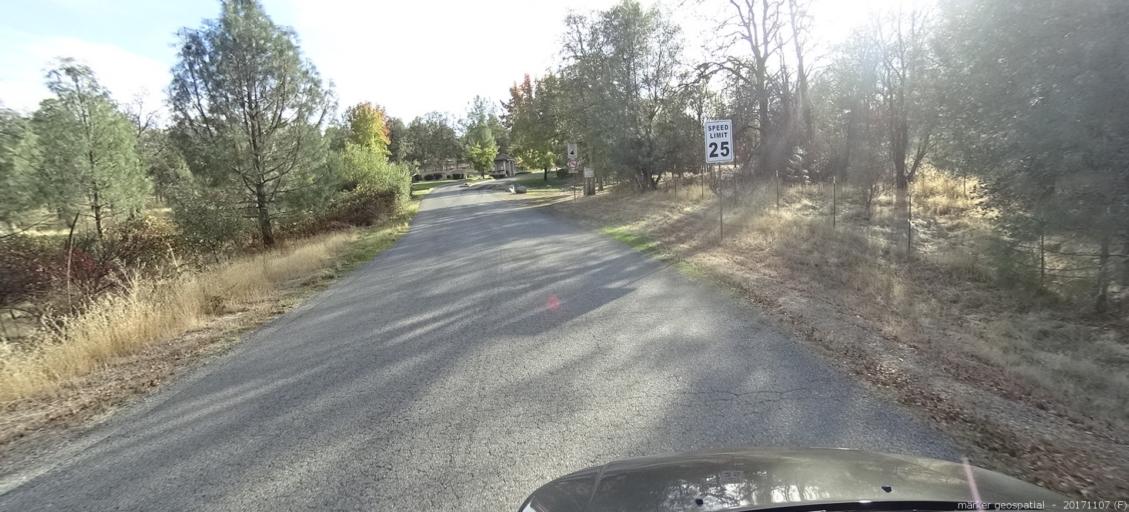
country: US
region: California
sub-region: Shasta County
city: Shasta
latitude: 40.5153
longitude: -122.4711
